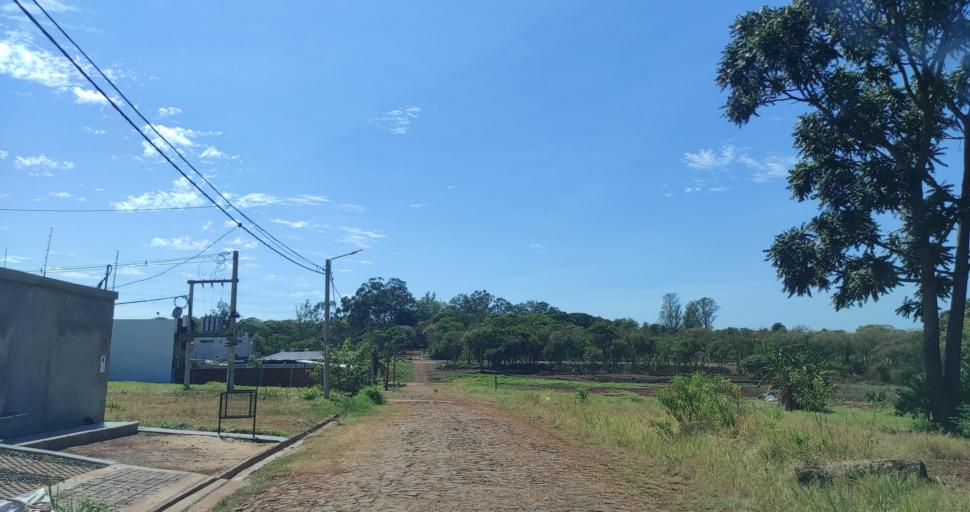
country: AR
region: Misiones
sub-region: Departamento de Capital
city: Posadas
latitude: -27.3934
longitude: -55.9265
